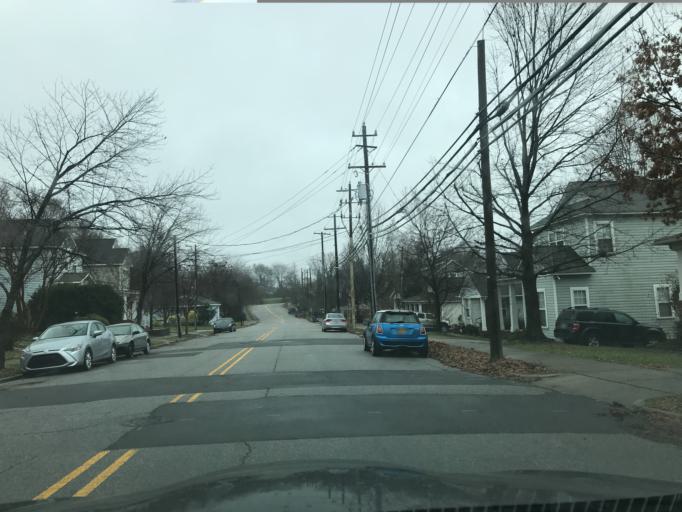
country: US
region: North Carolina
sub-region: Wake County
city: Raleigh
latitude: 35.7713
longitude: -78.6337
